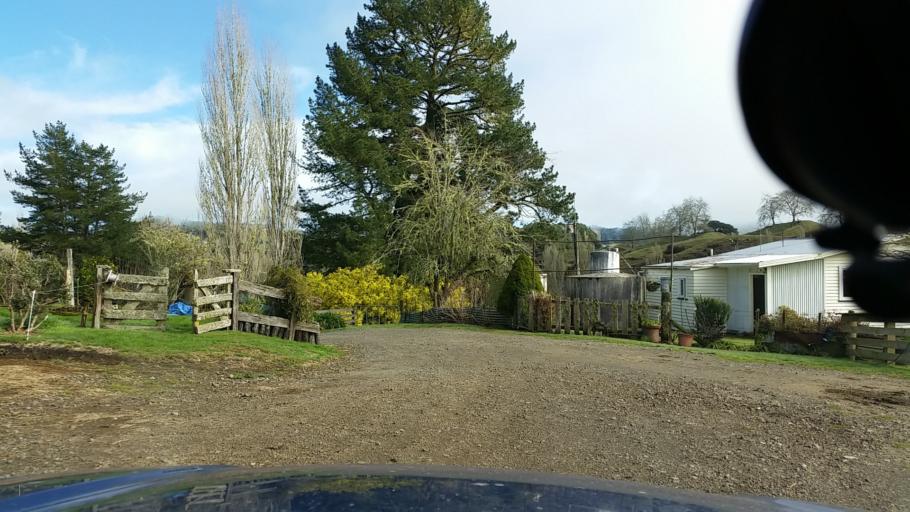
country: NZ
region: Taranaki
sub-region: New Plymouth District
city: Waitara
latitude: -39.0335
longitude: 174.8015
